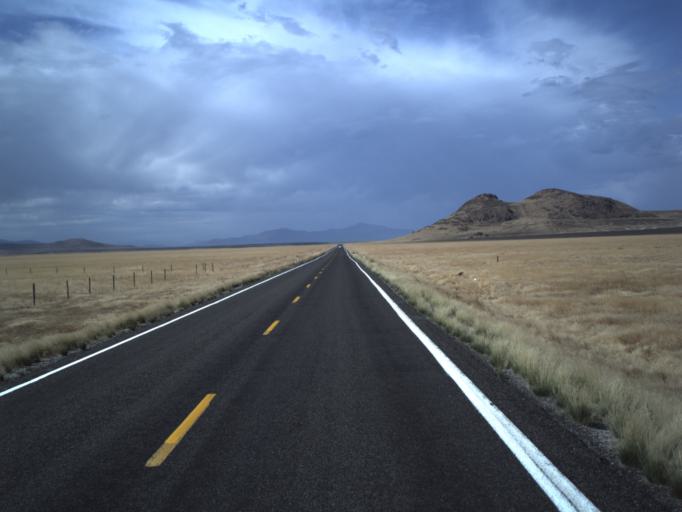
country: US
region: Utah
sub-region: Tooele County
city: Wendover
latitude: 41.3912
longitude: -113.9718
